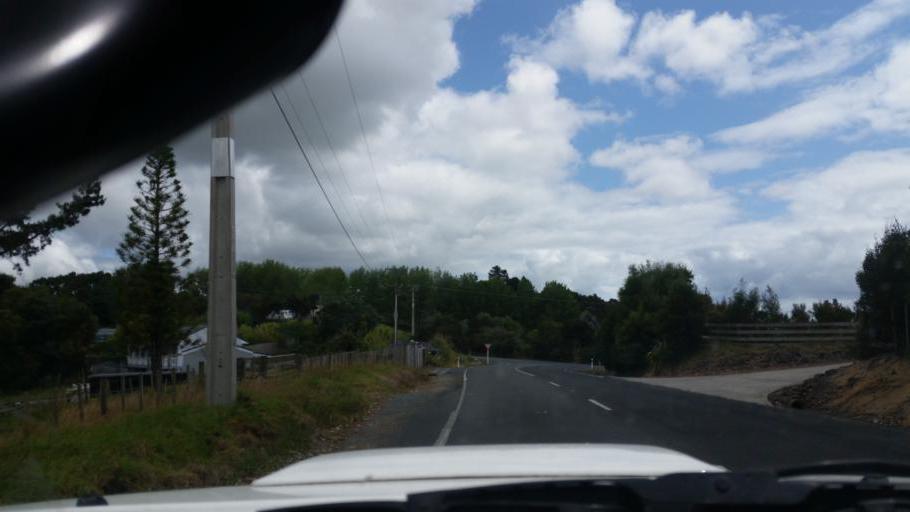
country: NZ
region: Auckland
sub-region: Auckland
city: Wellsford
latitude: -36.1322
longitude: 174.5561
